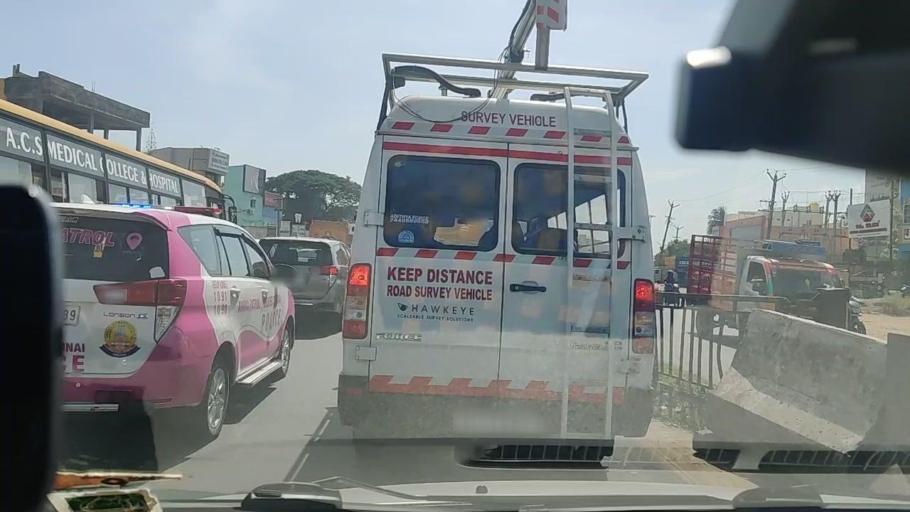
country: IN
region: Tamil Nadu
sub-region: Thiruvallur
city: Porur
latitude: 13.0621
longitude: 80.1497
